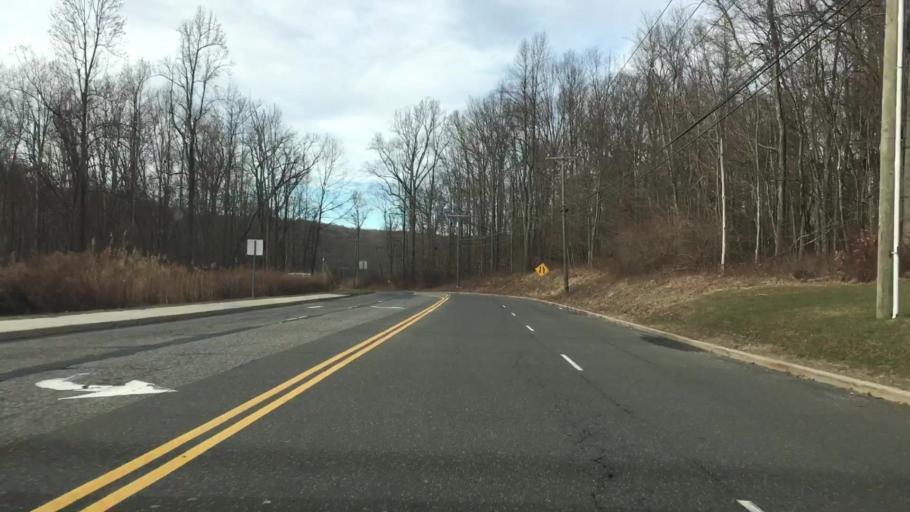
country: US
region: New York
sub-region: Putnam County
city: Peach Lake
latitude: 41.3828
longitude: -73.5368
